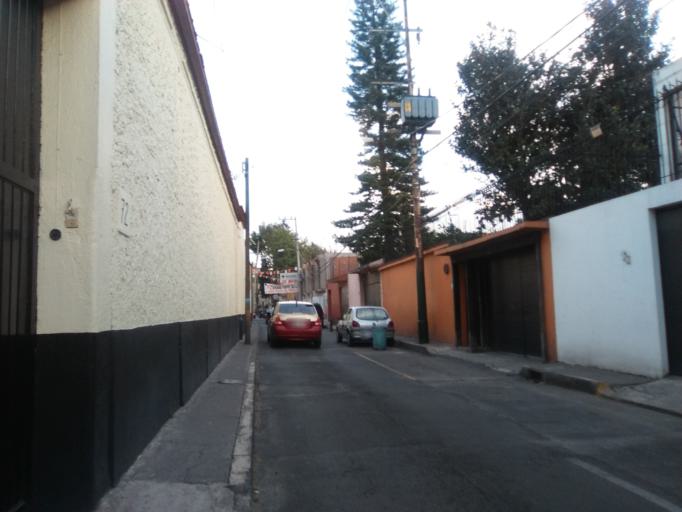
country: MX
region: Mexico City
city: Colonia del Valle
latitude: 19.3778
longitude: -99.1837
